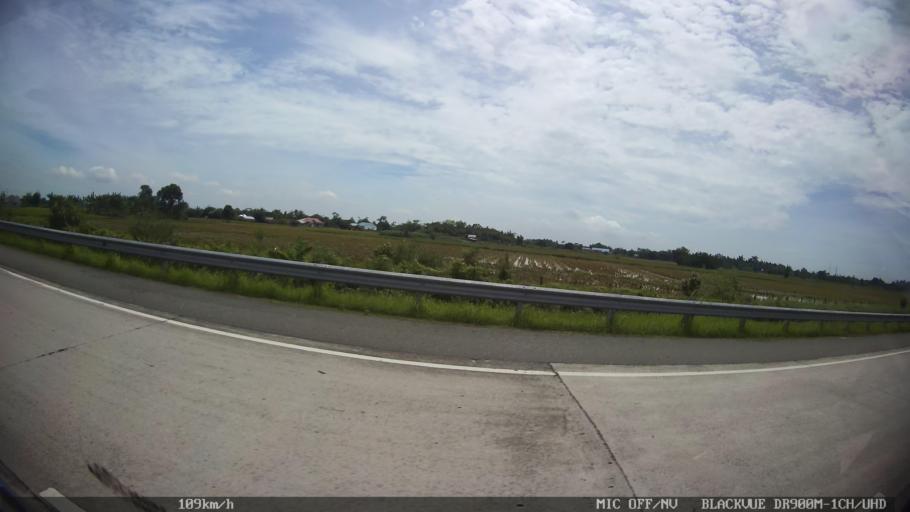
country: ID
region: North Sumatra
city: Percut
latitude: 3.5694
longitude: 98.8482
